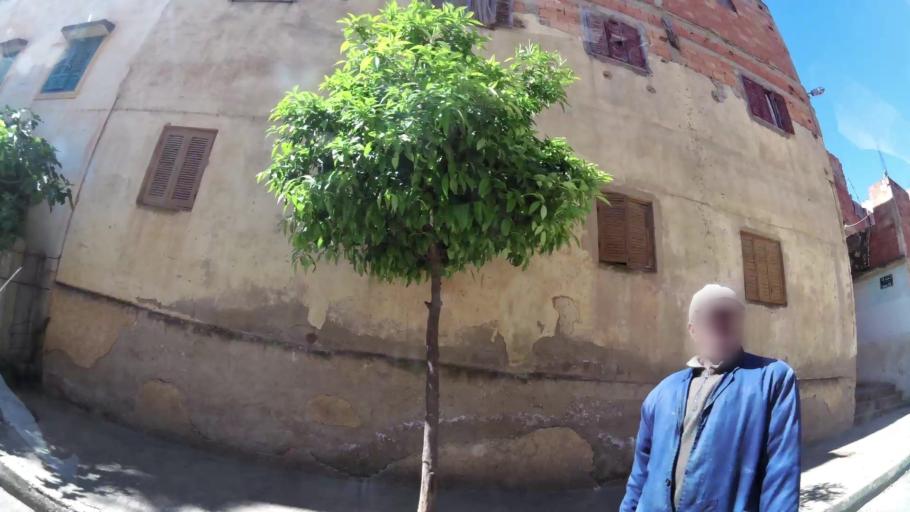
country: MA
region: Meknes-Tafilalet
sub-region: Meknes
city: Meknes
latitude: 33.9090
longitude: -5.5375
